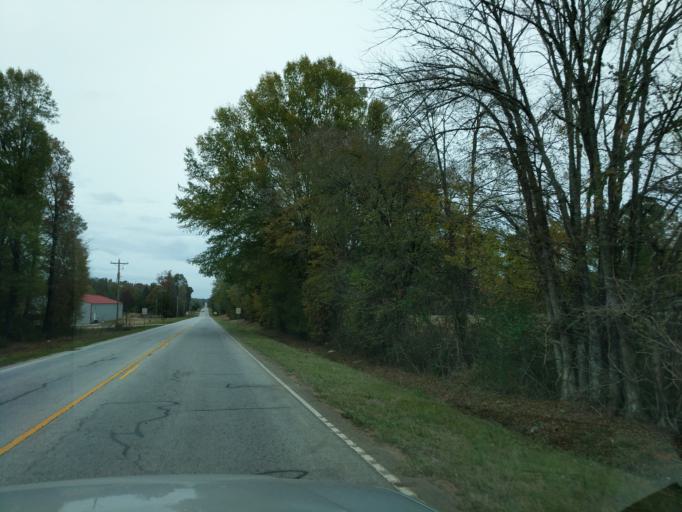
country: US
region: South Carolina
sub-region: Saluda County
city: Saluda
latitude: 34.0451
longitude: -81.7682
